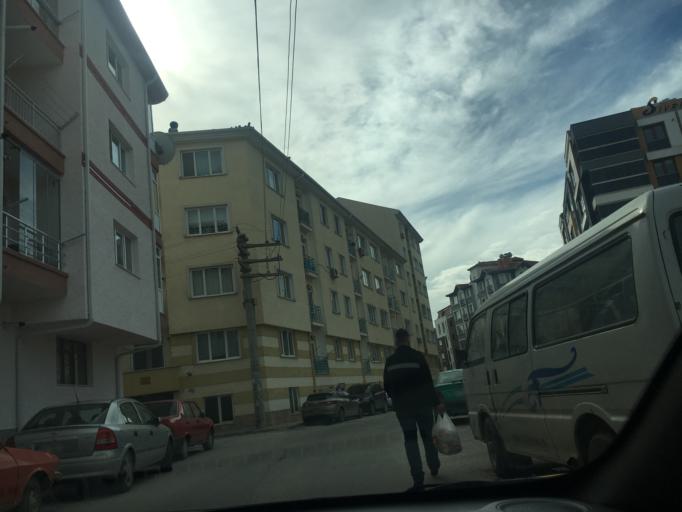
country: TR
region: Eskisehir
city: Eskisehir
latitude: 39.7738
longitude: 30.5043
